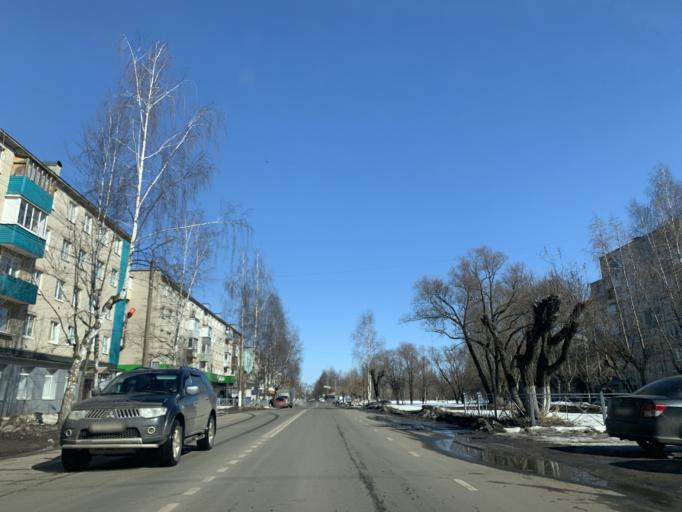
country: RU
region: Jaroslavl
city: Tutayev
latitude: 57.8681
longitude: 39.5116
